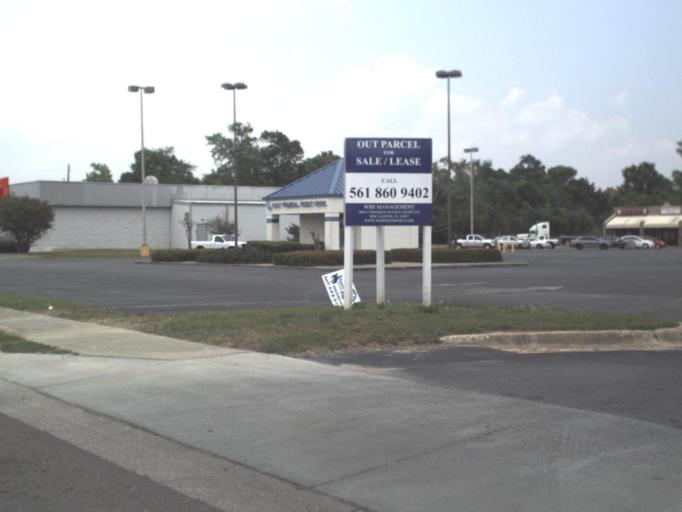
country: US
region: Florida
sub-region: Santa Rosa County
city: Milton
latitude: 30.6321
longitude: -87.0556
